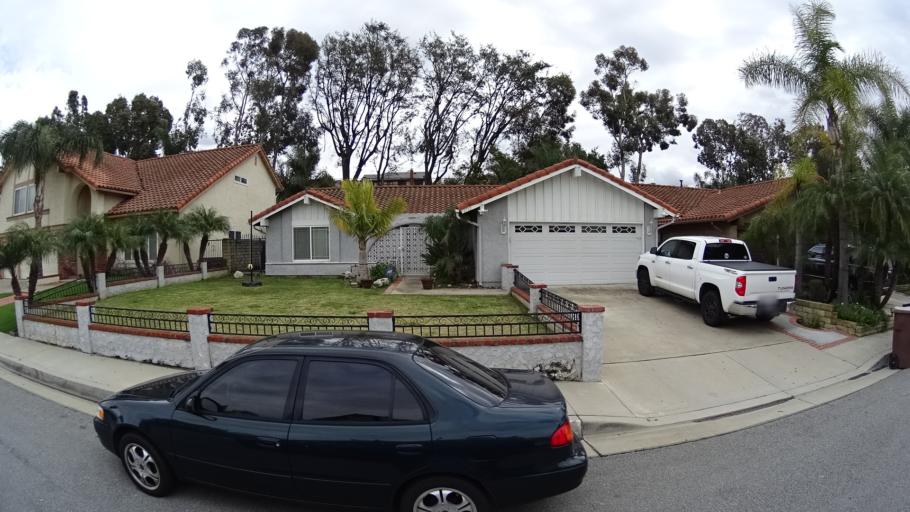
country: US
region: California
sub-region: Orange County
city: Villa Park
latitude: 33.8340
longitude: -117.7548
